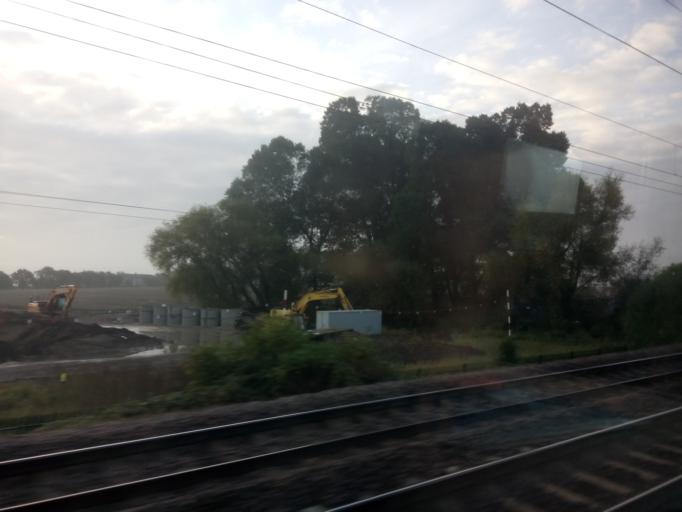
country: GB
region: England
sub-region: City of York
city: Copmanthorpe
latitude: 53.9159
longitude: -1.1332
